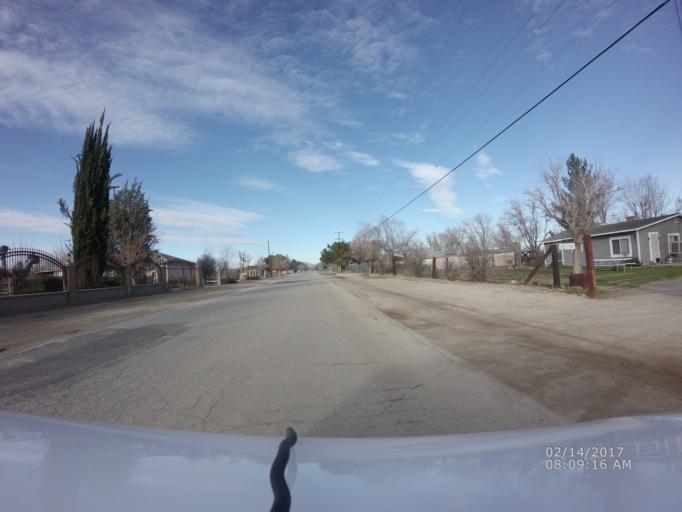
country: US
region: California
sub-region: Los Angeles County
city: Littlerock
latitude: 34.5538
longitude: -117.9479
